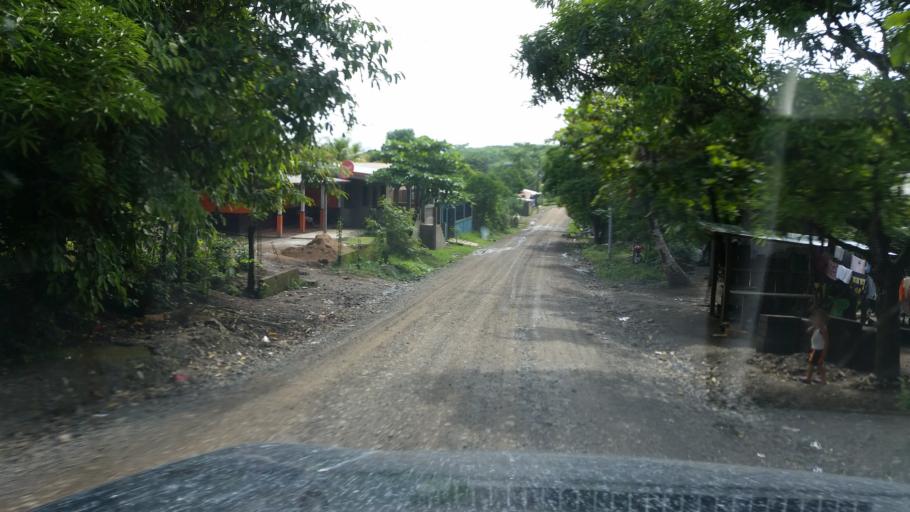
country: NI
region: Atlantico Norte (RAAN)
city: Siuna
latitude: 13.7159
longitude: -84.7694
